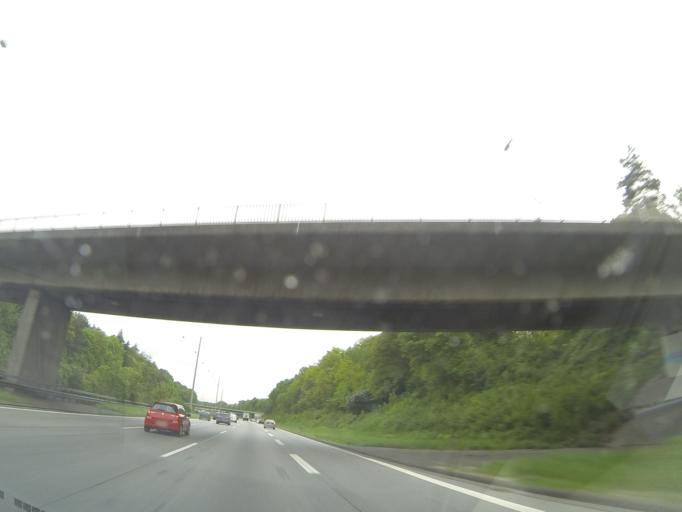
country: DE
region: Hamburg
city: Stellingen
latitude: 53.5729
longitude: 9.9038
